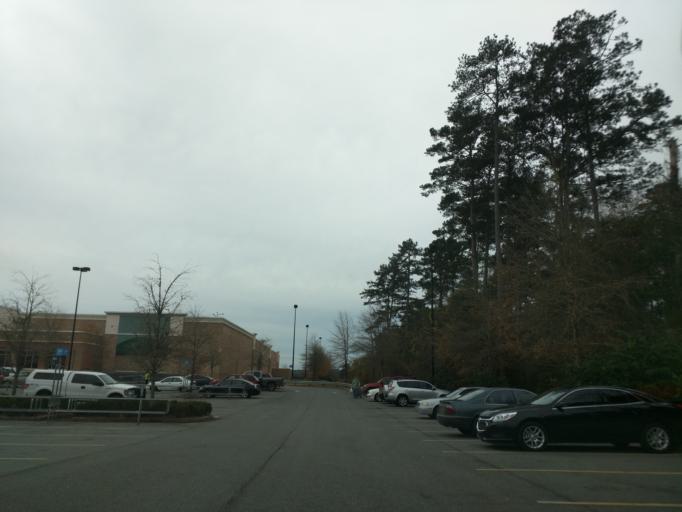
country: US
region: Florida
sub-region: Leon County
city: Tallahassee
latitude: 30.4620
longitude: -84.2183
